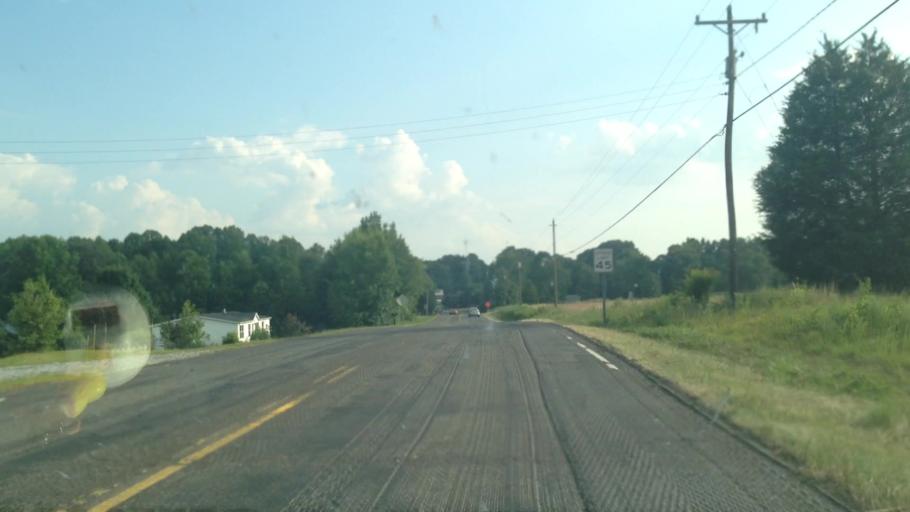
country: US
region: North Carolina
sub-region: Forsyth County
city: Kernersville
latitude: 36.0633
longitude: -80.0636
